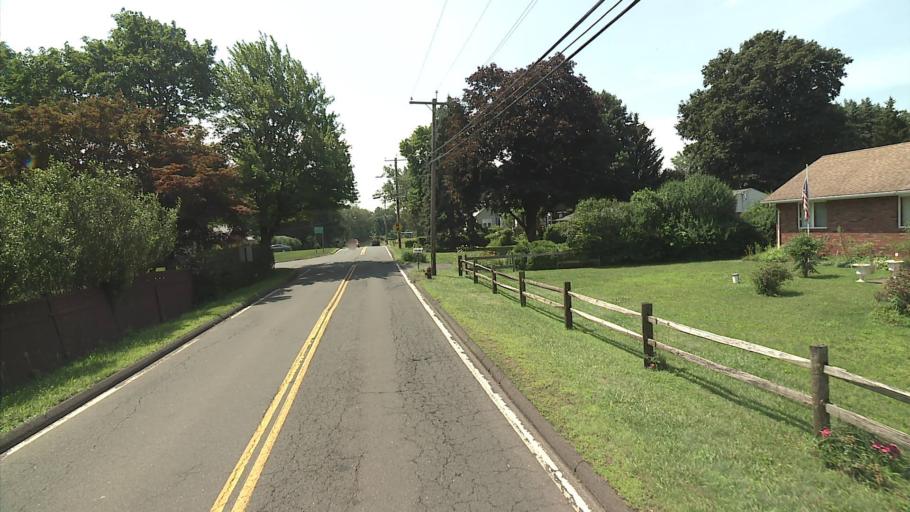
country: US
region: Connecticut
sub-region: Middlesex County
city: Middletown
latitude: 41.5494
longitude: -72.7010
